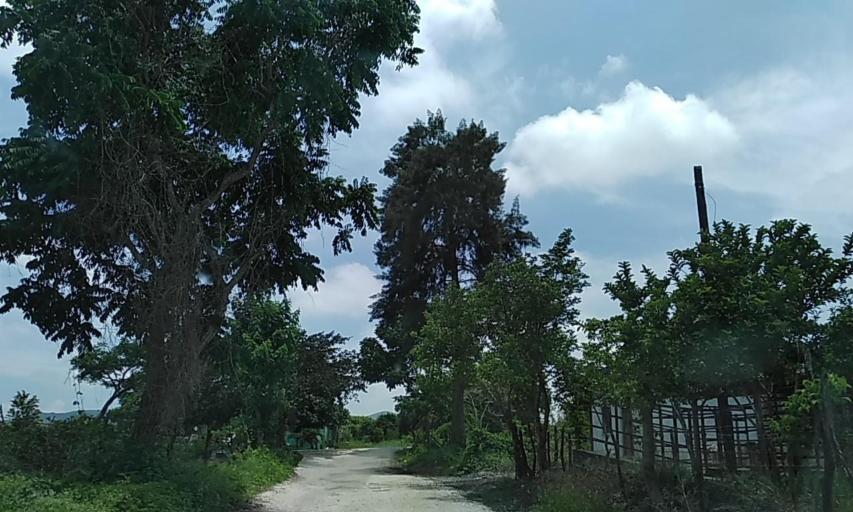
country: MX
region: Veracruz
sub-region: Emiliano Zapata
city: Dos Rios
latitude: 19.4440
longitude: -96.7602
